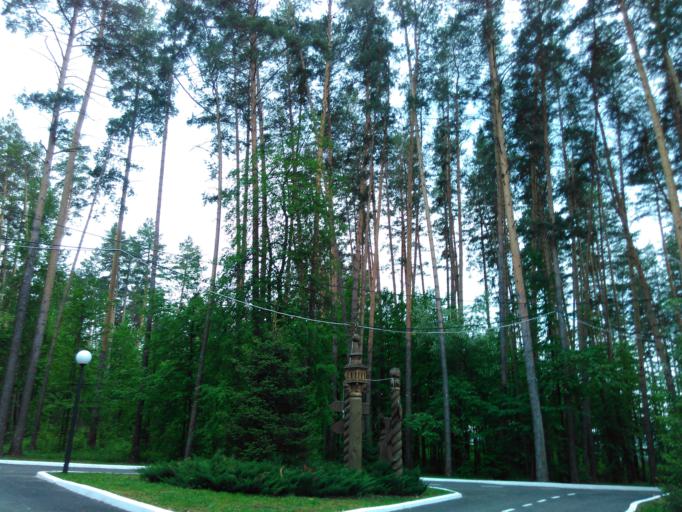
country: RU
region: Tatarstan
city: Al'met'yevsk
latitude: 54.9519
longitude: 52.2640
